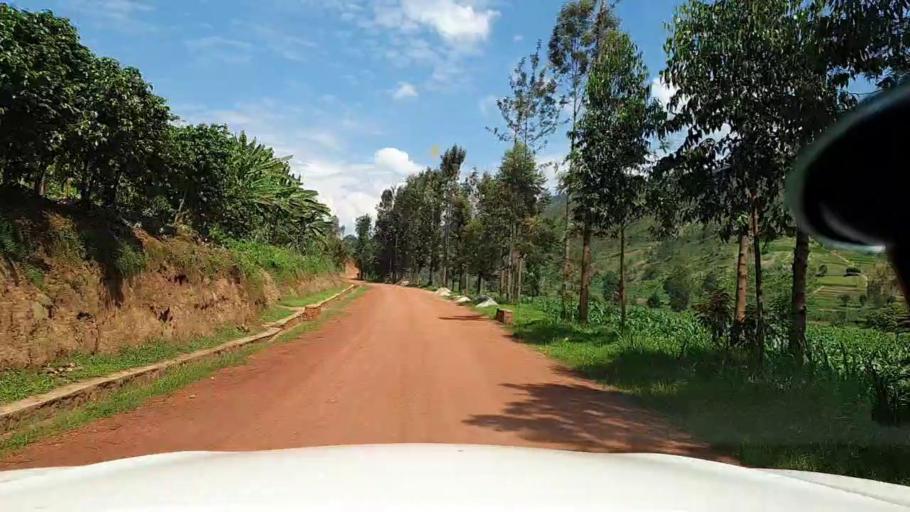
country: RW
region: Kigali
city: Kigali
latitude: -1.7913
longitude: 29.8843
